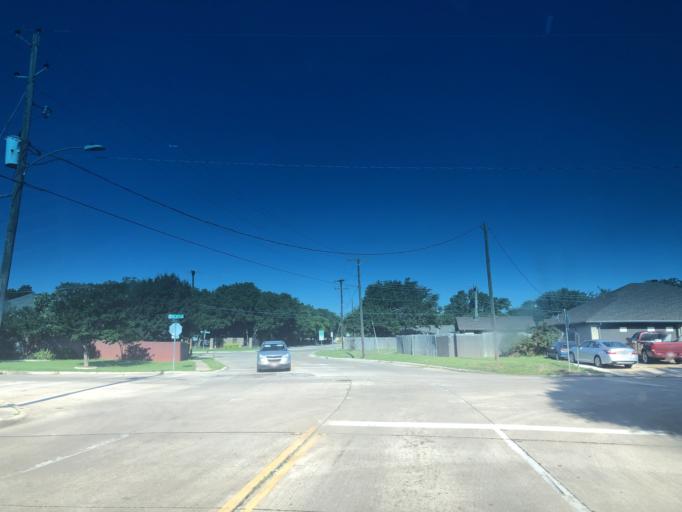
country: US
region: Texas
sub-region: Dallas County
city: Grand Prairie
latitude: 32.7135
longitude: -97.0015
